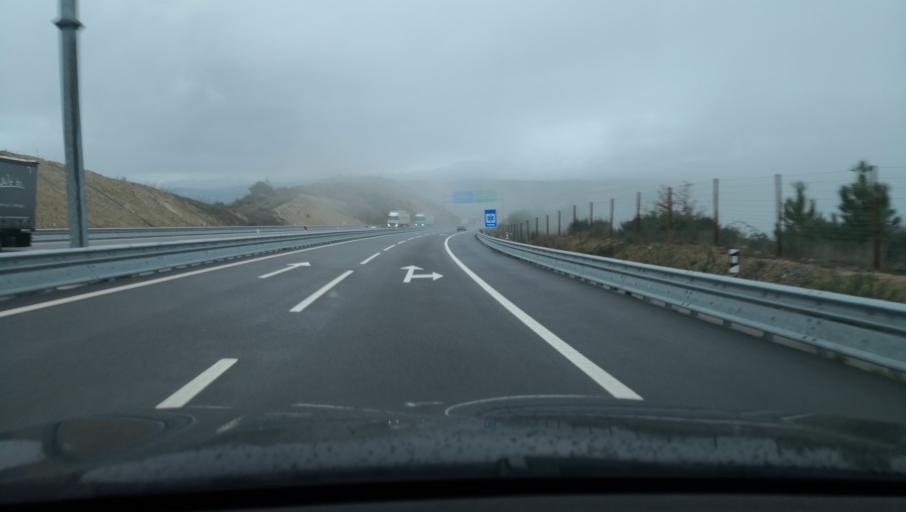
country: PT
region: Vila Real
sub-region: Vila Real
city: Vila Real
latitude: 41.2733
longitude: -7.7778
